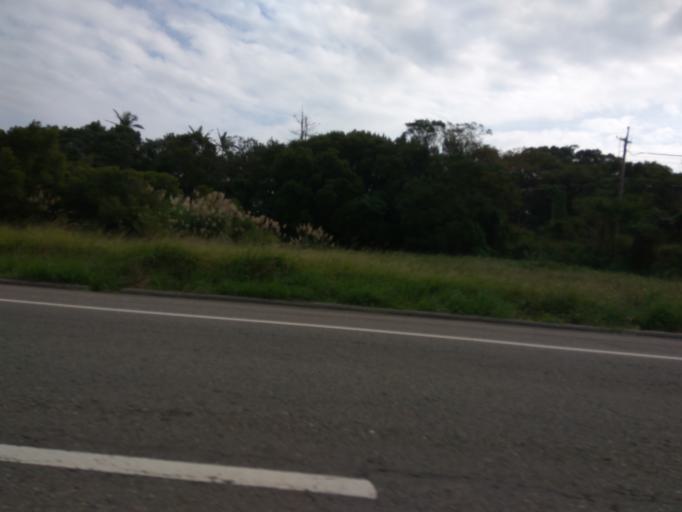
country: TW
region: Taiwan
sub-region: Hsinchu
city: Zhubei
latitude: 24.9571
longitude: 121.0127
